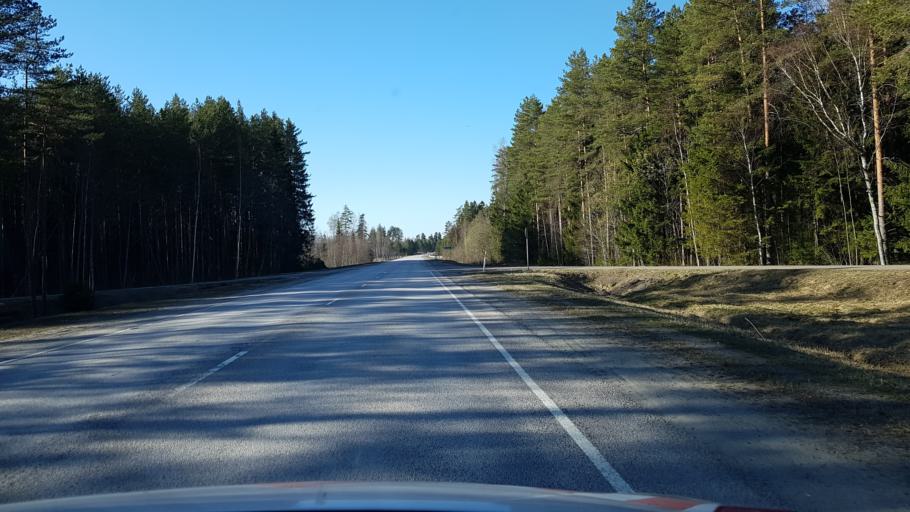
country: EE
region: Ida-Virumaa
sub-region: Johvi vald
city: Johvi
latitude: 59.1569
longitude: 27.3568
